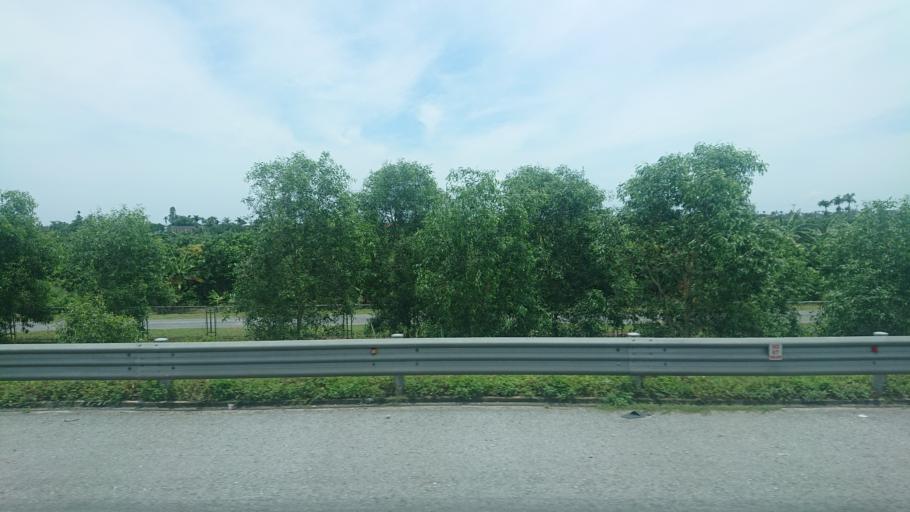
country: VN
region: Hai Duong
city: Tu Ky
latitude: 20.8259
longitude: 106.4626
